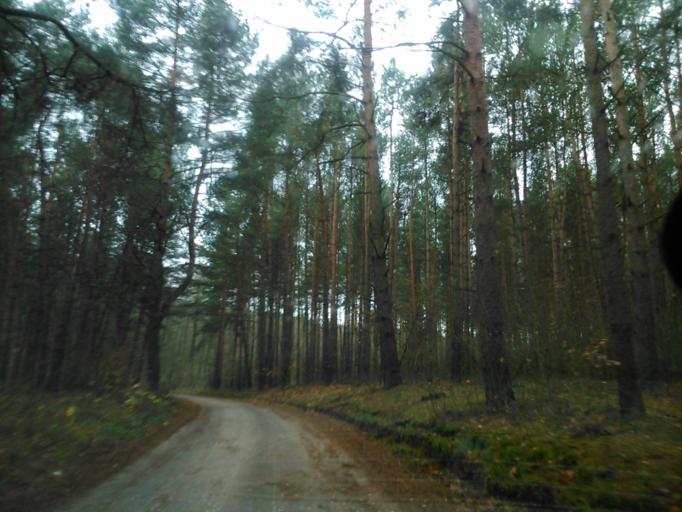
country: PL
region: Kujawsko-Pomorskie
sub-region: Powiat golubsko-dobrzynski
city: Golub-Dobrzyn
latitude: 53.1126
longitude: 19.0968
